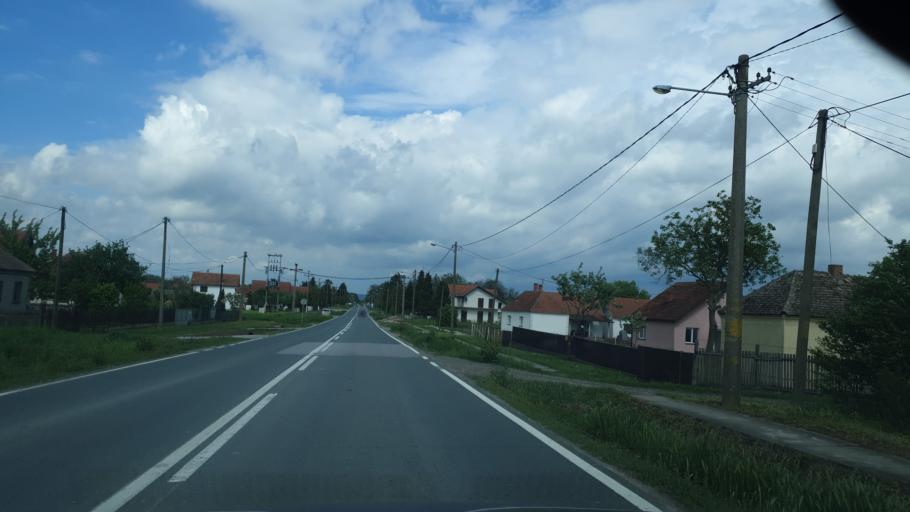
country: RS
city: Stubline
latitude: 44.5418
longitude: 20.1275
